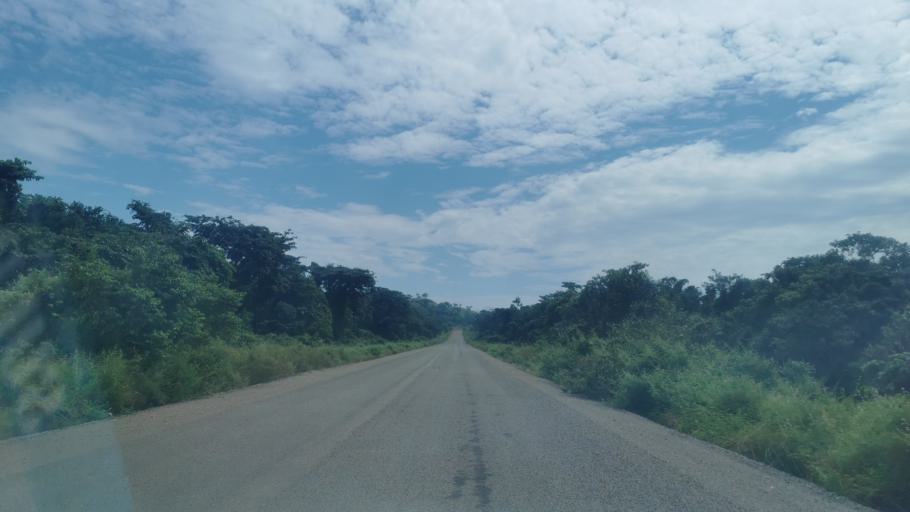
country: ET
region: Gambela
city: Gambela
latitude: 7.6165
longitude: 34.6982
